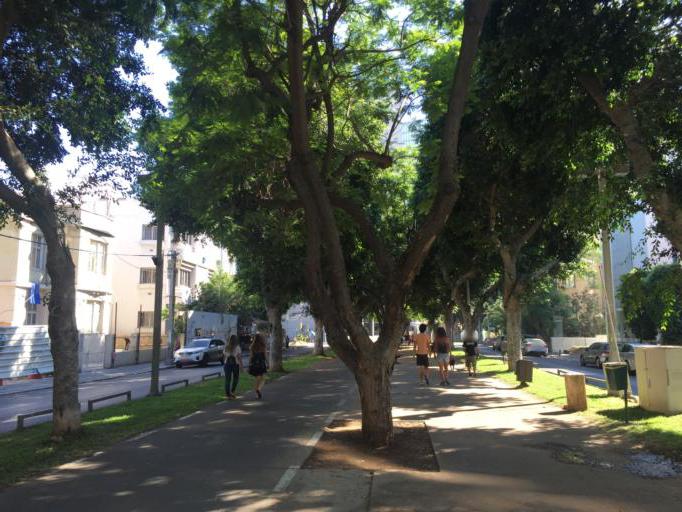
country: IL
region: Tel Aviv
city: Tel Aviv
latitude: 32.0651
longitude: 34.7763
